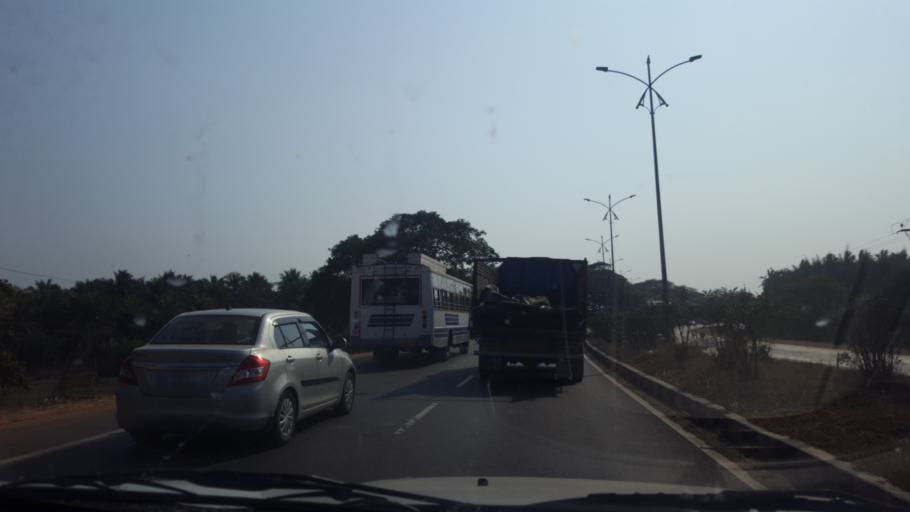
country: IN
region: Andhra Pradesh
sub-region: Vishakhapatnam
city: Anakapalle
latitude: 17.6796
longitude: 83.0263
